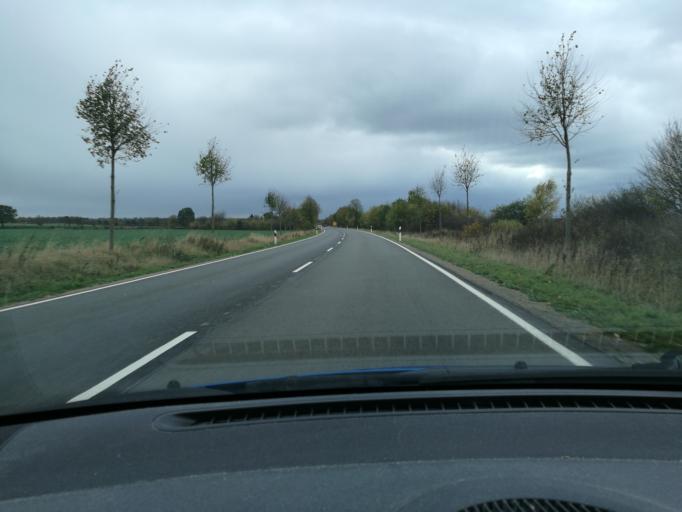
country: DE
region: Schleswig-Holstein
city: Harmsdorf
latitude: 53.6939
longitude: 10.7304
